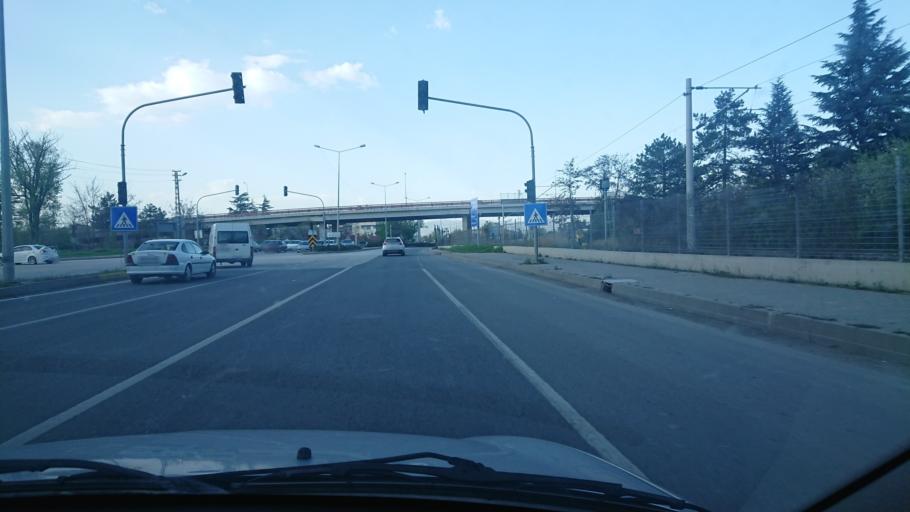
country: TR
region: Eskisehir
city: Eskisehir
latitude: 39.7676
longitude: 30.4803
